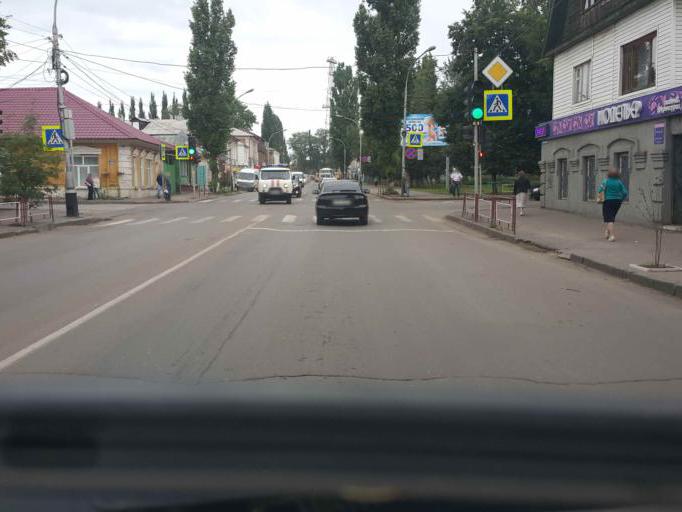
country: RU
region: Tambov
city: Michurinsk
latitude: 52.8926
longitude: 40.5019
